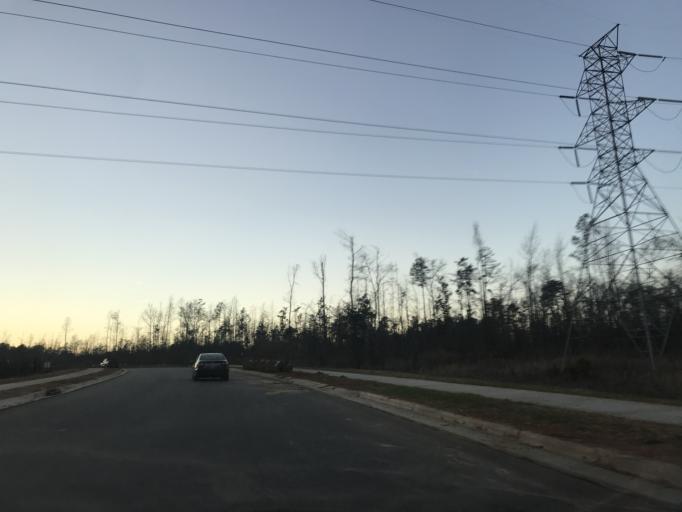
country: US
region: North Carolina
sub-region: Wake County
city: Raleigh
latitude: 35.8718
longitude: -78.5714
